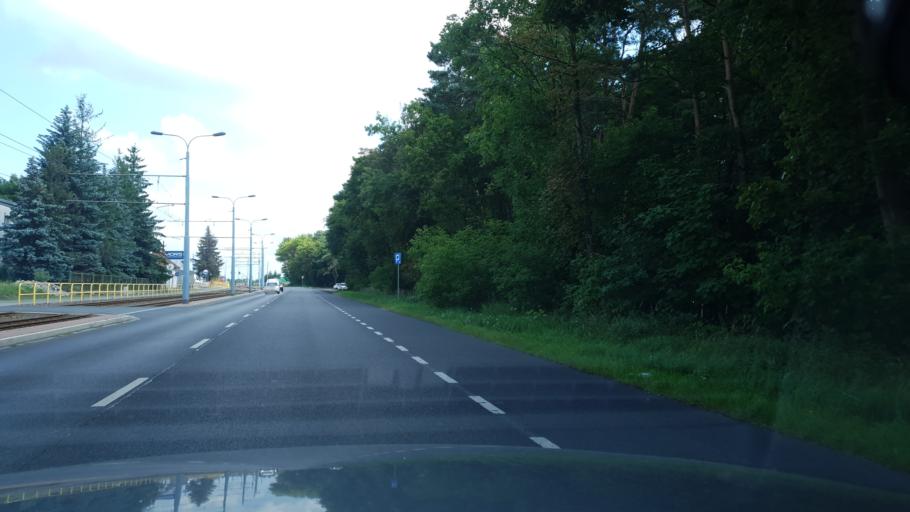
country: PL
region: Kujawsko-Pomorskie
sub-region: Grudziadz
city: Grudziadz
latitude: 53.4571
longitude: 18.7376
